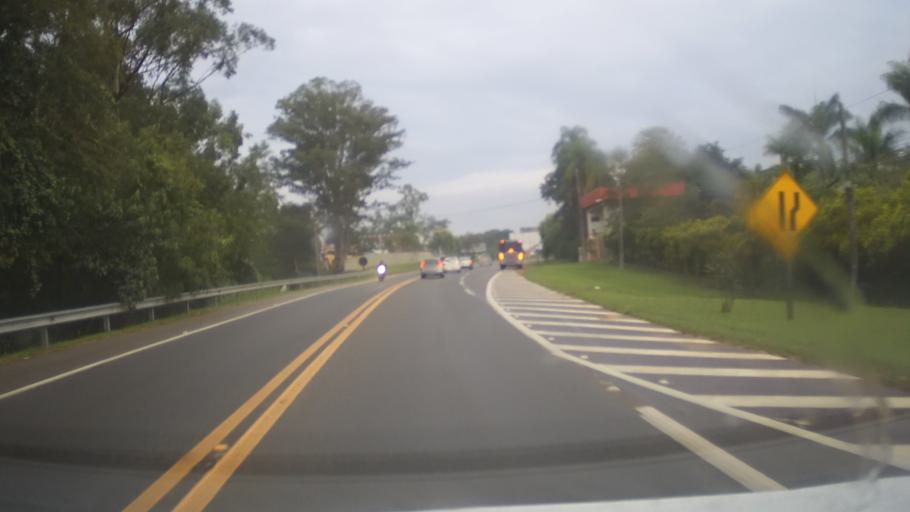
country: BR
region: Sao Paulo
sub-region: Valinhos
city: Valinhos
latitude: -22.9356
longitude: -46.9737
